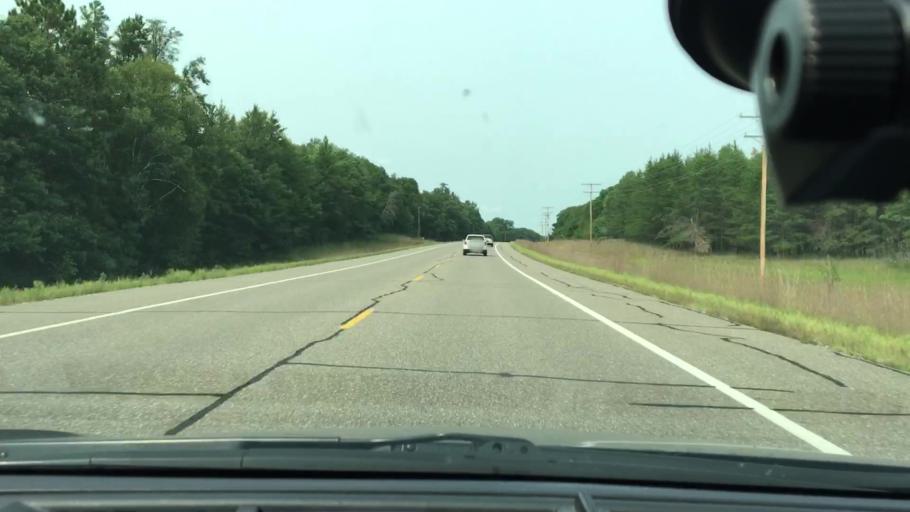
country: US
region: Minnesota
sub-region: Crow Wing County
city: Cross Lake
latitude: 46.6062
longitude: -94.1312
